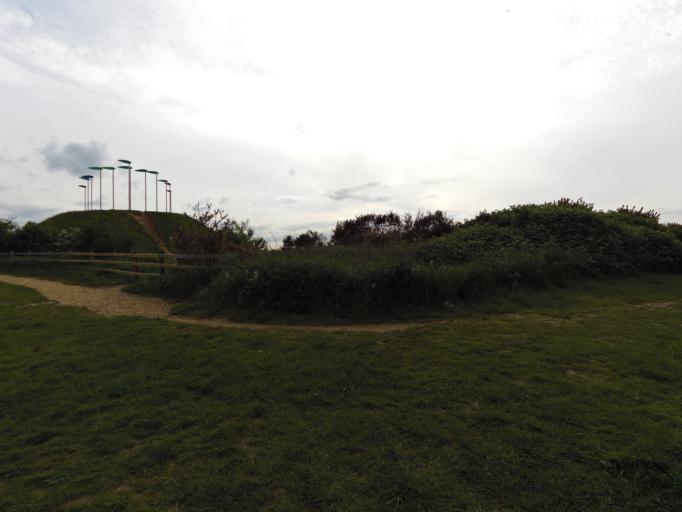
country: GB
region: England
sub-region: Suffolk
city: Ipswich
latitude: 52.0259
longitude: 1.1906
